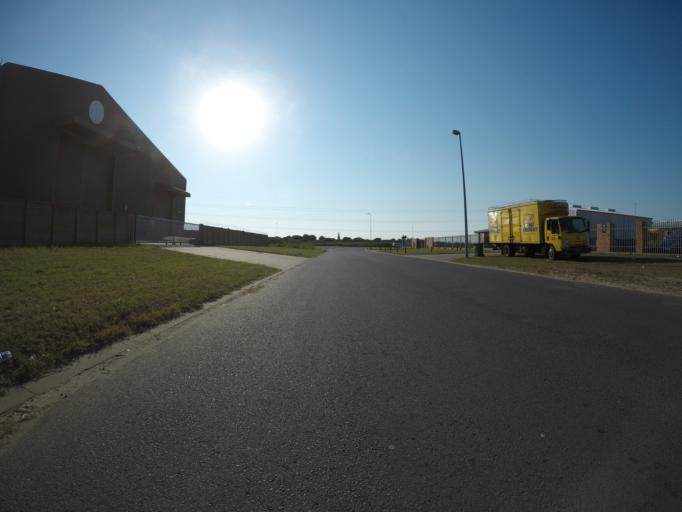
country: ZA
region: KwaZulu-Natal
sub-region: uThungulu District Municipality
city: Richards Bay
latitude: -28.7347
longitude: 32.0375
